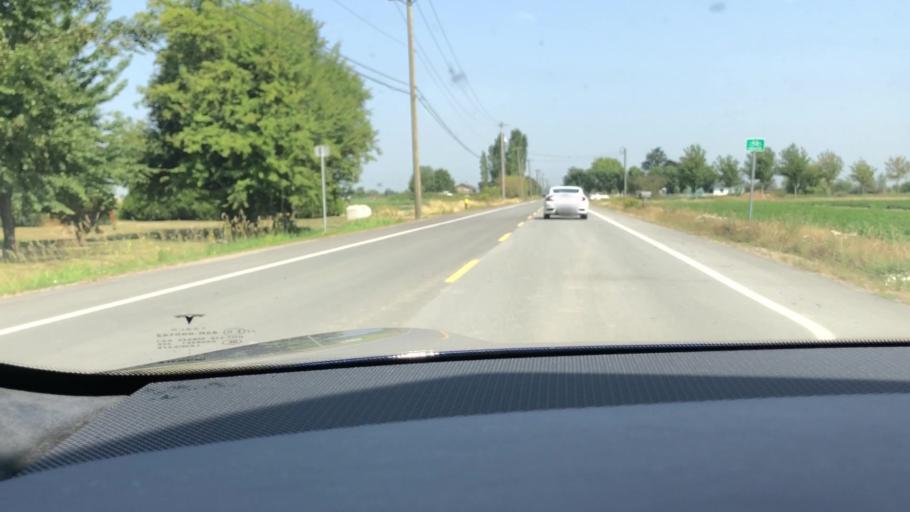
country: CA
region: British Columbia
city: Ladner
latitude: 49.0452
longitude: -123.0796
